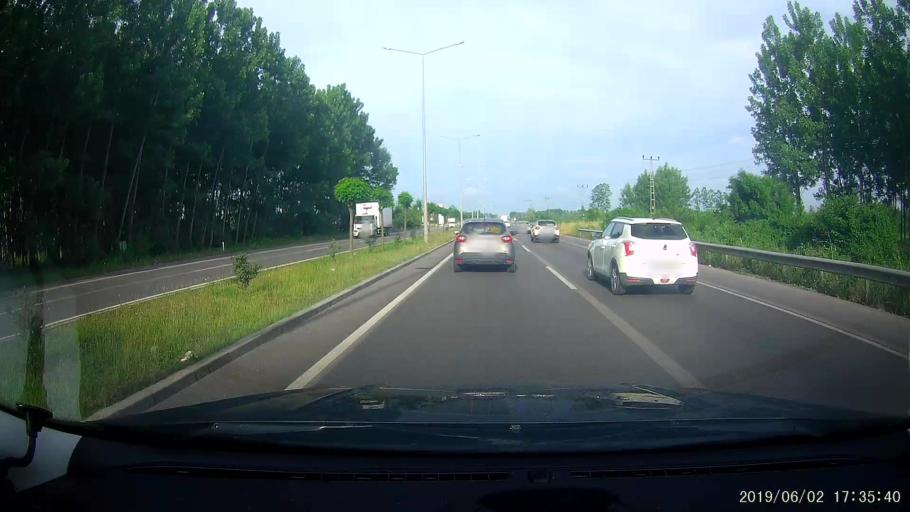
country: TR
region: Samsun
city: Terme
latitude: 41.2195
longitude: 36.8865
